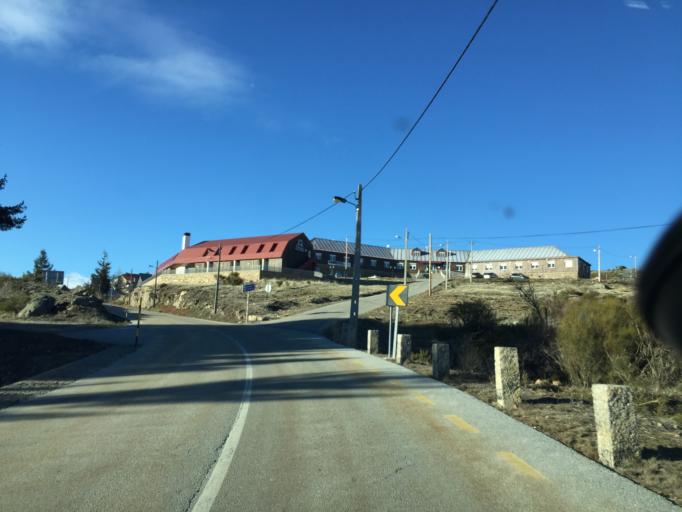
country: PT
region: Castelo Branco
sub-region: Covilha
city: Covilha
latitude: 40.3094
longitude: -7.5503
